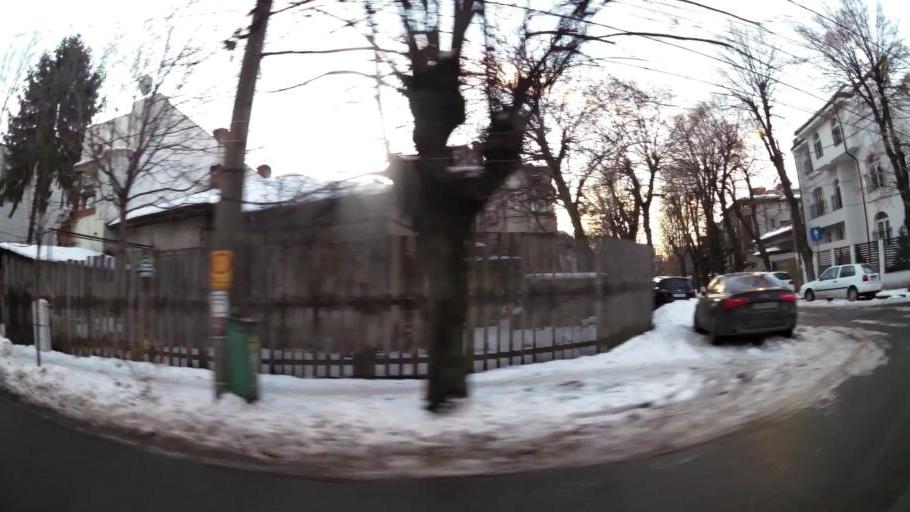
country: RO
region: Ilfov
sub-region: Comuna Fundeni-Dobroesti
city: Fundeni
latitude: 44.4350
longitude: 26.1411
